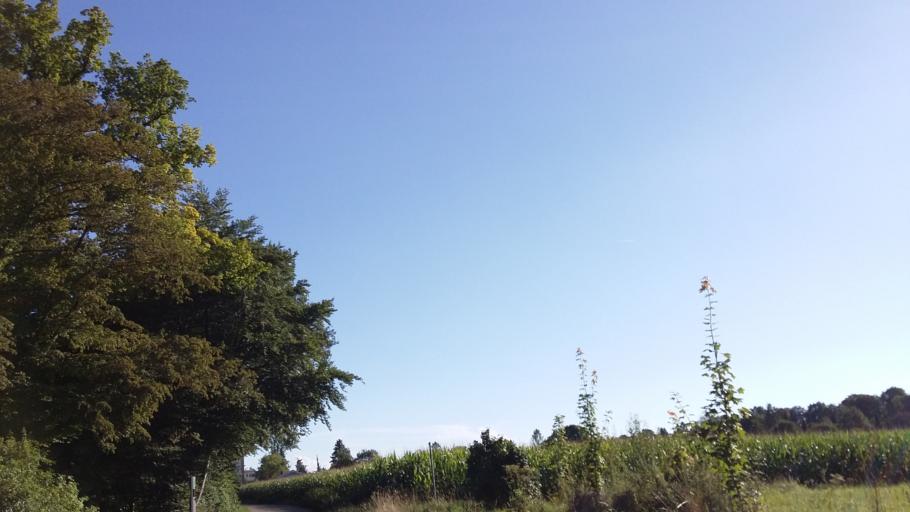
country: DE
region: Bavaria
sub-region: Upper Bavaria
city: Gauting
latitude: 48.0767
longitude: 11.3898
